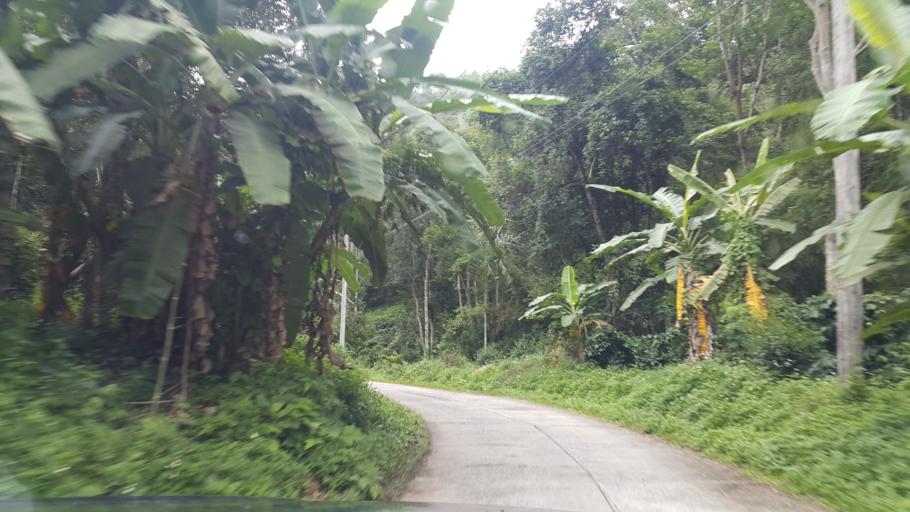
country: TH
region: Lampang
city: Wang Nuea
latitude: 19.0790
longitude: 99.3863
